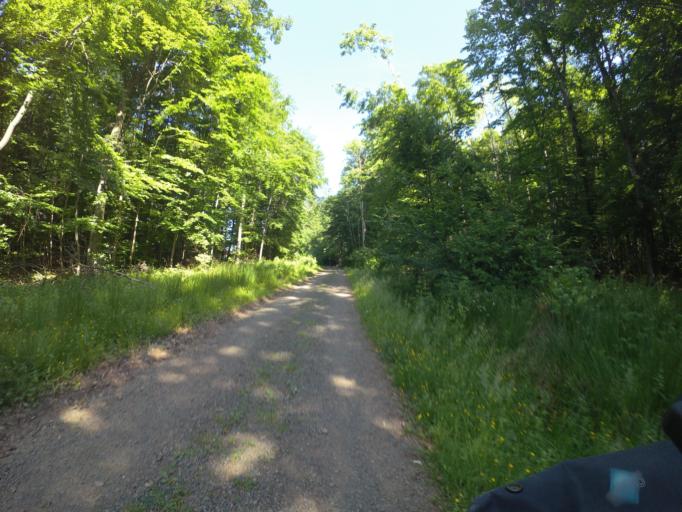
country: DE
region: Rheinland-Pfalz
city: Dunzweiler
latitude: 49.3836
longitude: 7.2815
